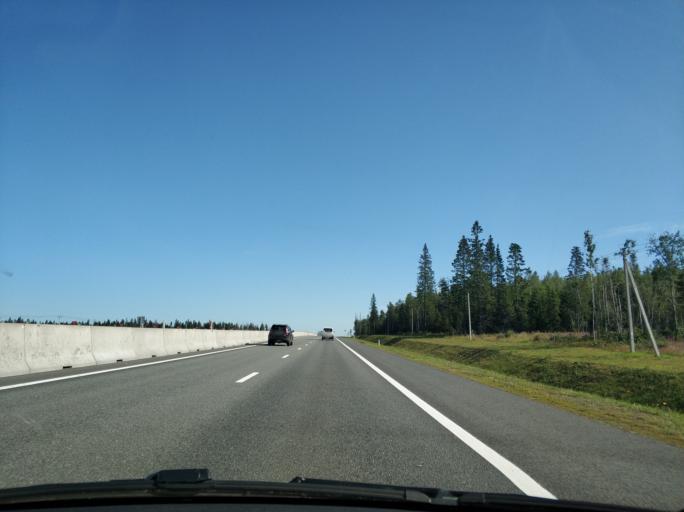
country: RU
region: Leningrad
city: Sosnovo
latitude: 60.4869
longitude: 30.1958
